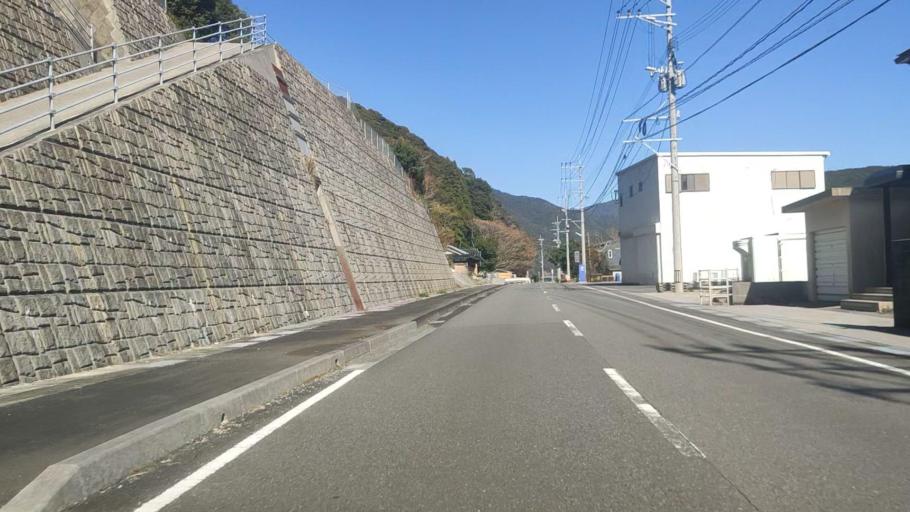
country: JP
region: Oita
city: Saiki
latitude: 32.8290
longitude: 131.9593
